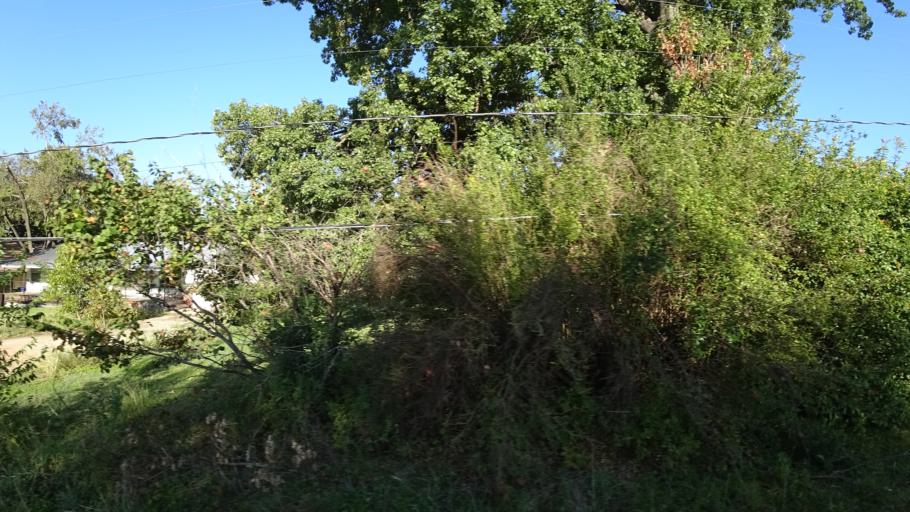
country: US
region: Texas
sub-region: Travis County
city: Wells Branch
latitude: 30.3555
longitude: -97.6929
